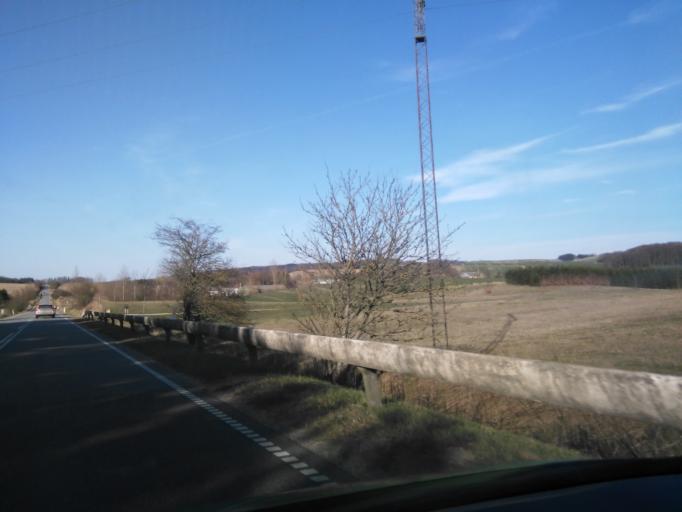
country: DK
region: Central Jutland
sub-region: Skanderborg Kommune
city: Ry
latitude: 55.9767
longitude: 9.7586
